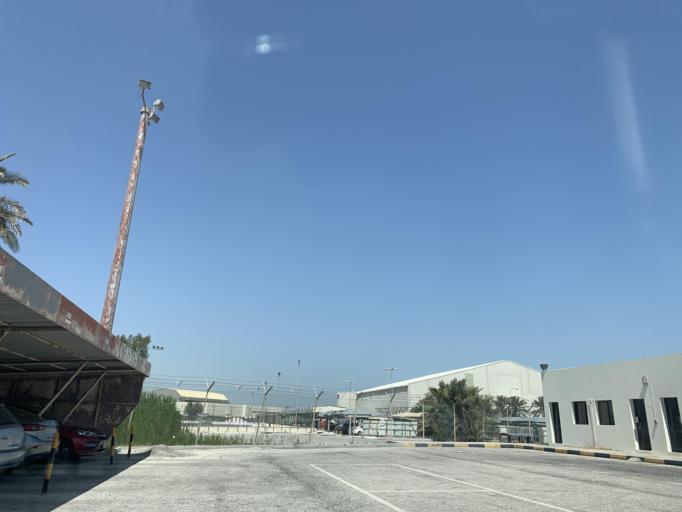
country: BH
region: Muharraq
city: Al Muharraq
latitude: 26.2718
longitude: 50.6195
